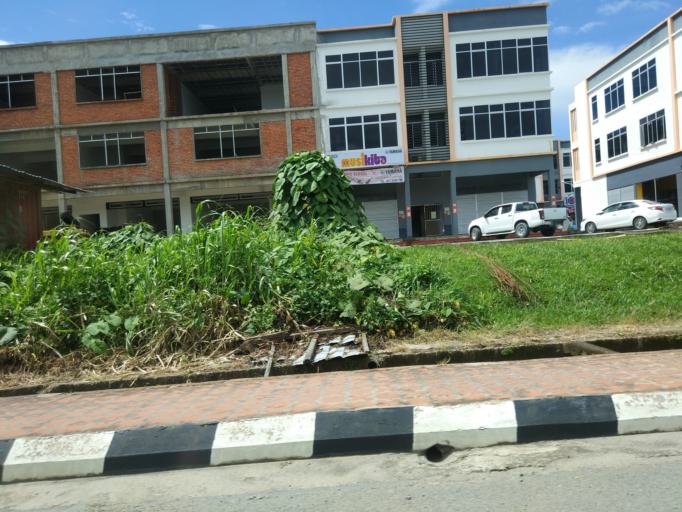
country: BN
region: Temburong
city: Bangar
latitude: 4.8591
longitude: 115.4055
